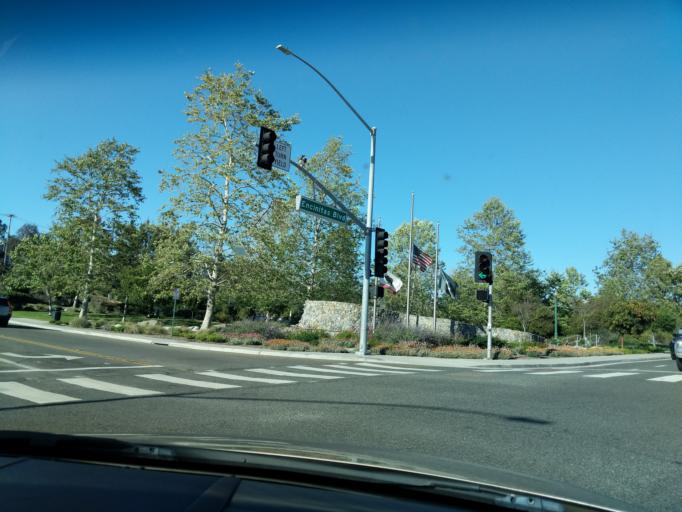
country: US
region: California
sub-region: San Diego County
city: Encinitas
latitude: 33.0489
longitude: -117.2931
